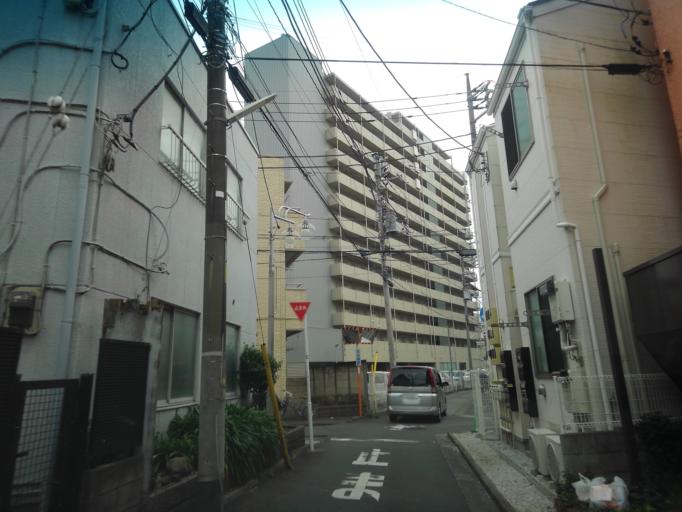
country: JP
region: Tokyo
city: Hino
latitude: 35.7014
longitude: 139.4171
